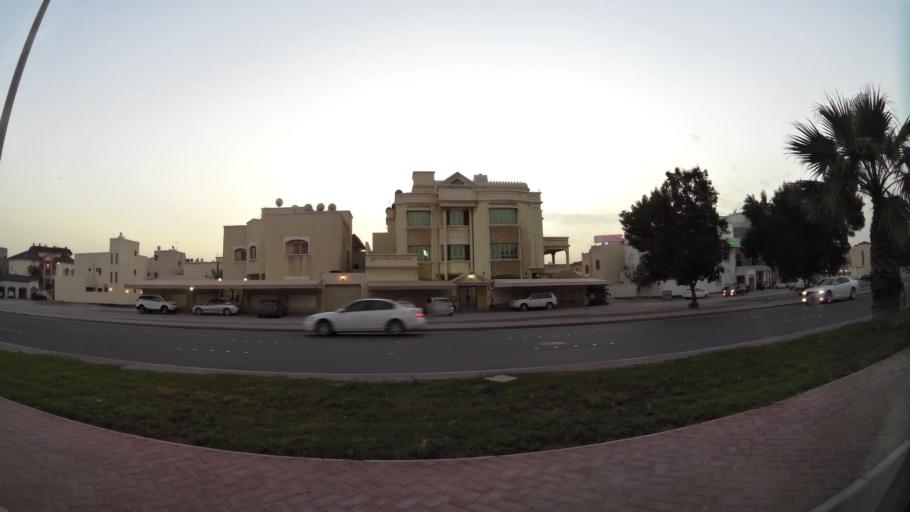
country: BH
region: Manama
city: Manama
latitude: 26.2079
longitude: 50.5671
